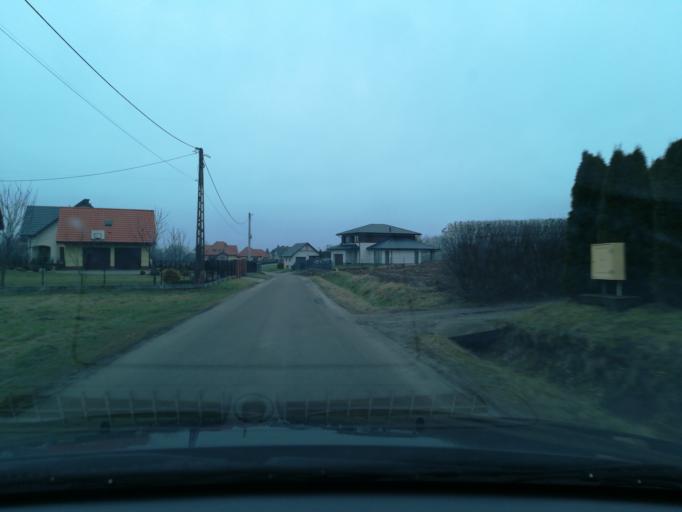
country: PL
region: Subcarpathian Voivodeship
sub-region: Powiat lancucki
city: Kosina
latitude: 50.0733
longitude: 22.3343
